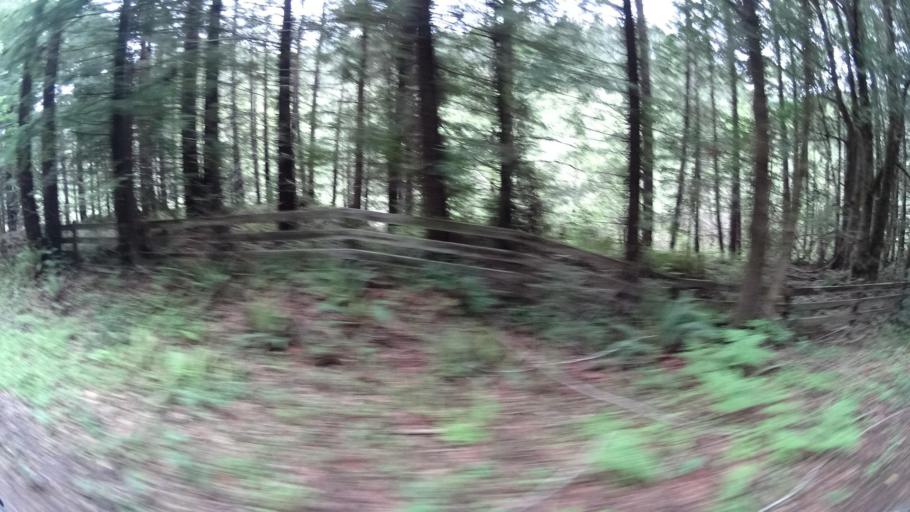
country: US
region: California
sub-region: Humboldt County
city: Blue Lake
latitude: 40.9616
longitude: -123.8392
